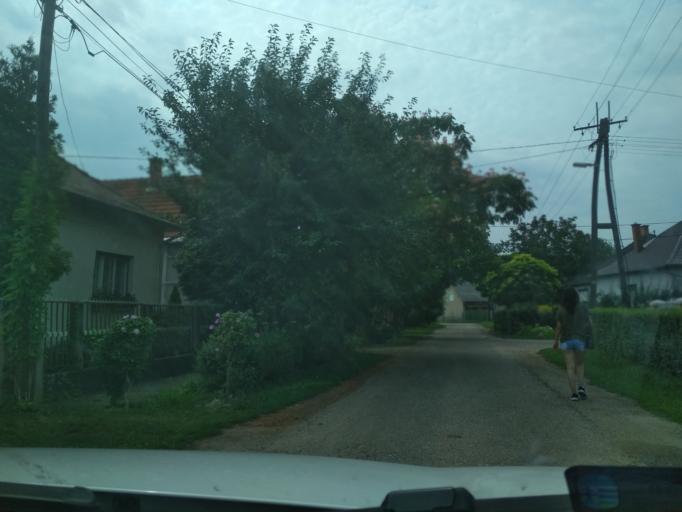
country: HU
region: Jasz-Nagykun-Szolnok
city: Tiszafured
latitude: 47.6200
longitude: 20.7532
